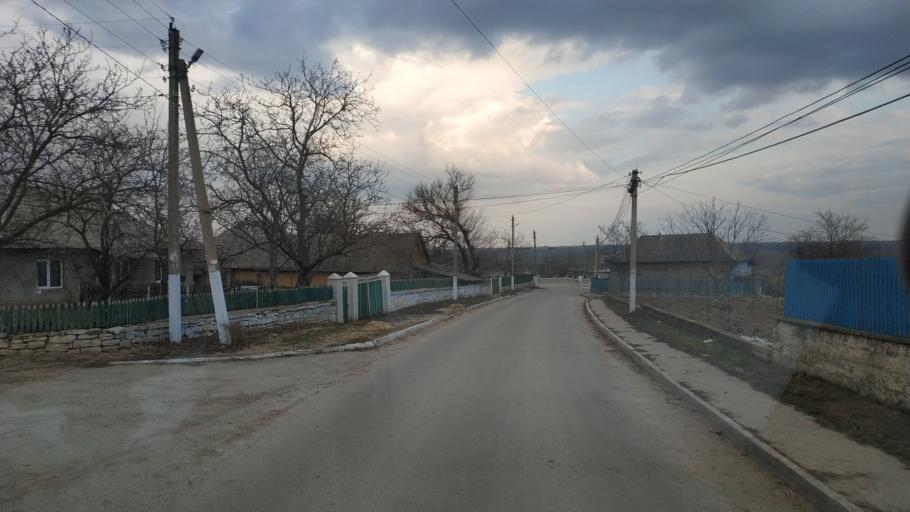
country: MD
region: Telenesti
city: Grigoriopol
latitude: 47.0268
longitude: 29.3538
